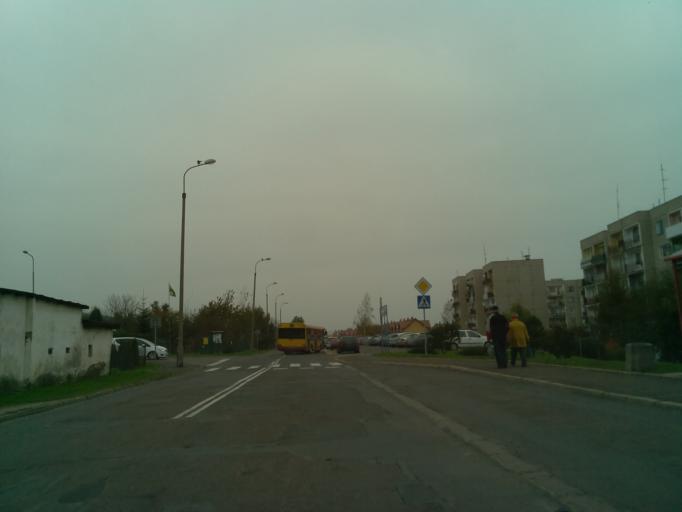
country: PL
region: Lower Silesian Voivodeship
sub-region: Powiat swidnicki
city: Swiebodzice
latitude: 50.8641
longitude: 16.3100
